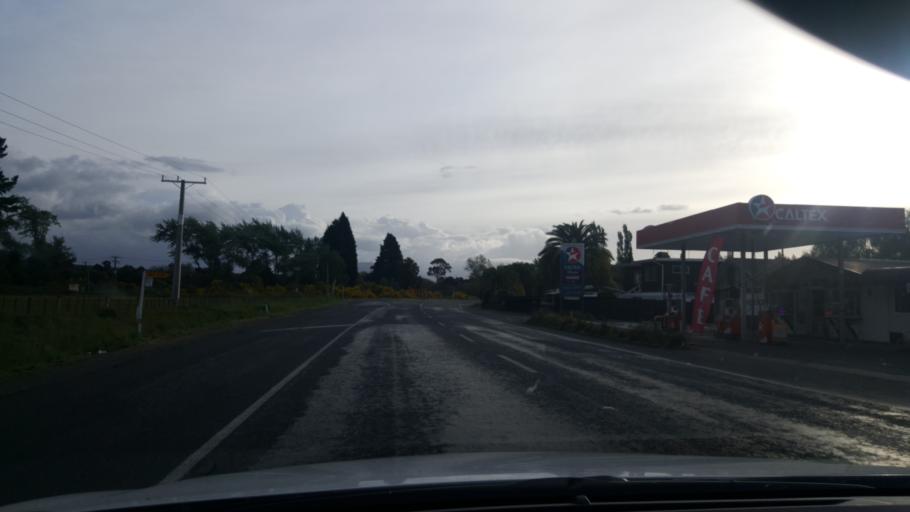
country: NZ
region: Waikato
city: Turangi
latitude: -38.9109
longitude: 175.9037
